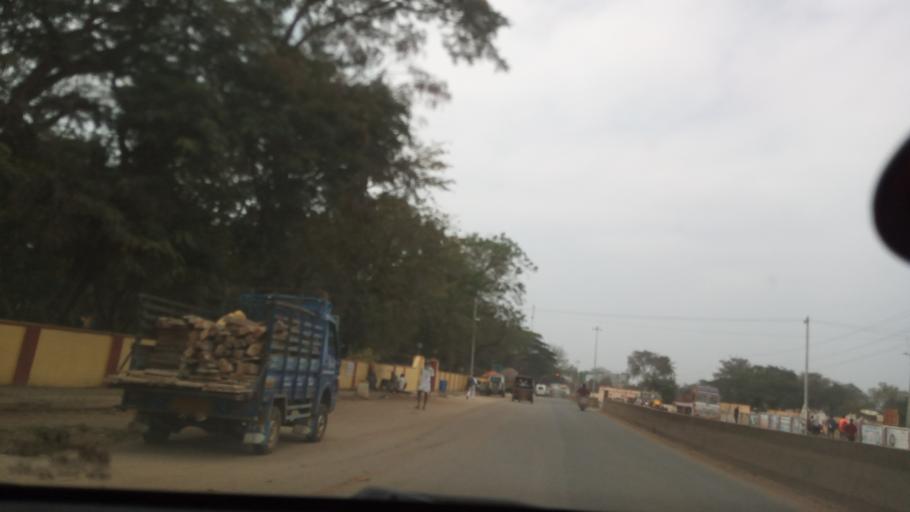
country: IN
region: Karnataka
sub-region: Chamrajnagar
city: Chamrajnagar
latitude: 11.9198
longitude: 76.9395
